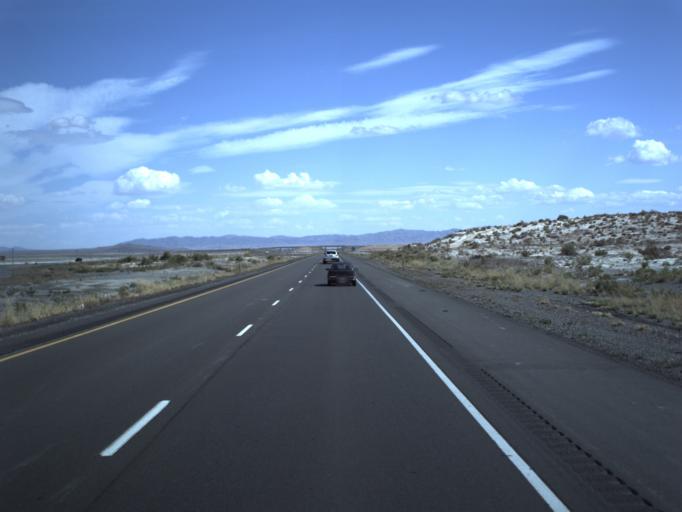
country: US
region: Utah
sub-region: Tooele County
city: Wendover
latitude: 40.7267
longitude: -113.2821
